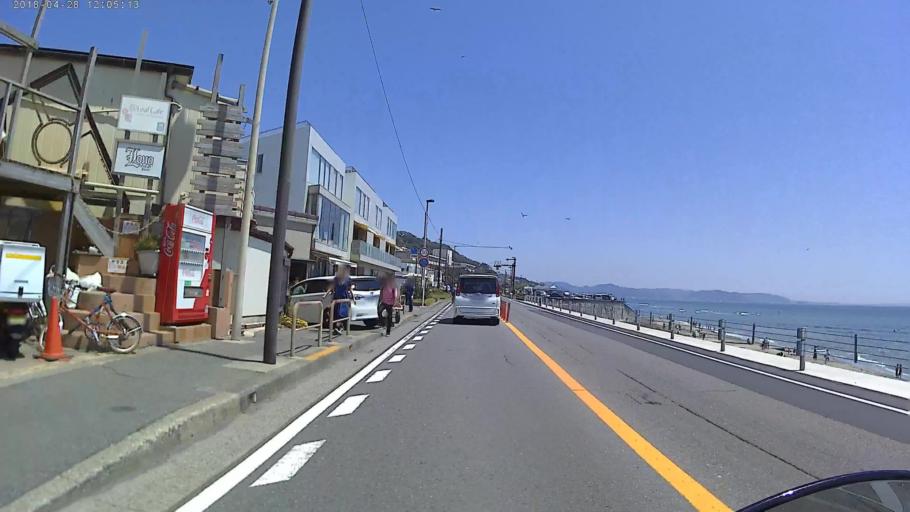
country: JP
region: Kanagawa
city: Kamakura
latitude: 35.3055
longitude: 139.5094
